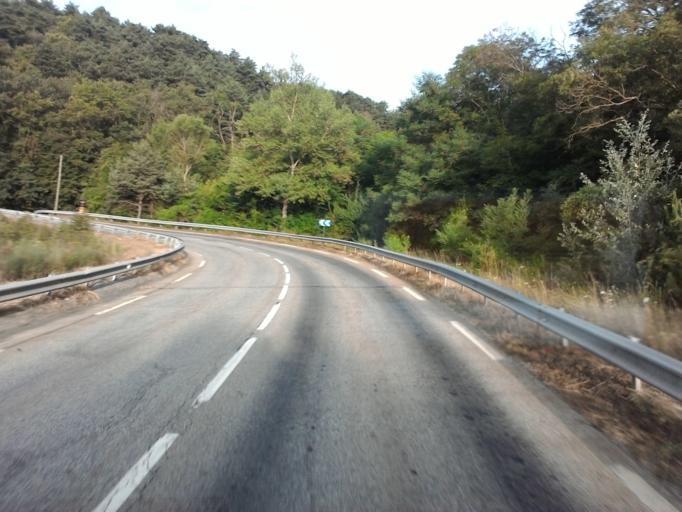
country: FR
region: Rhone-Alpes
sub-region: Departement de l'Isere
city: La Mure
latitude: 44.8992
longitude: 5.8128
